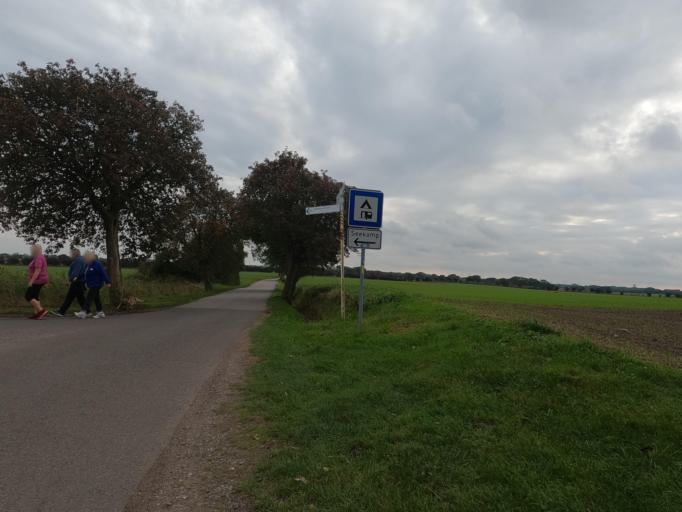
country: DE
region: Schleswig-Holstein
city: Neukirchen
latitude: 54.3443
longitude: 11.0497
